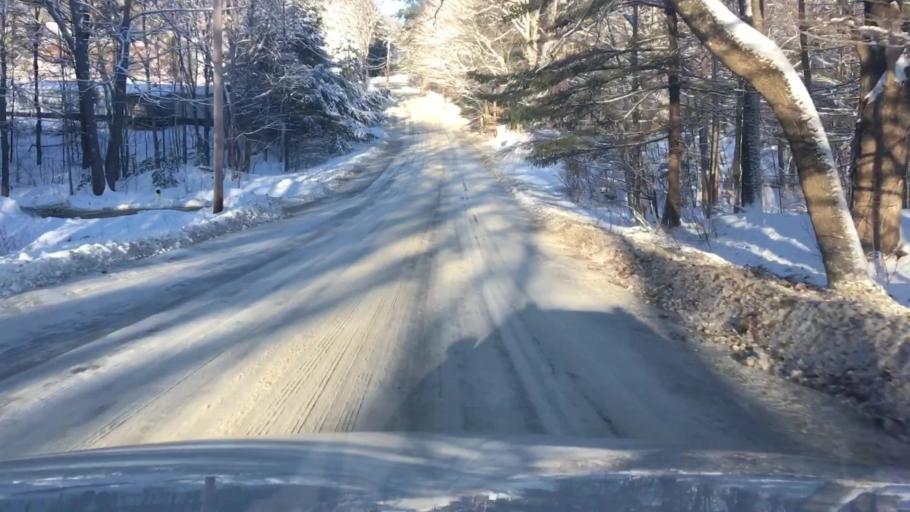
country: US
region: Maine
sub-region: Kennebec County
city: Readfield
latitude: 44.4149
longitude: -69.9184
